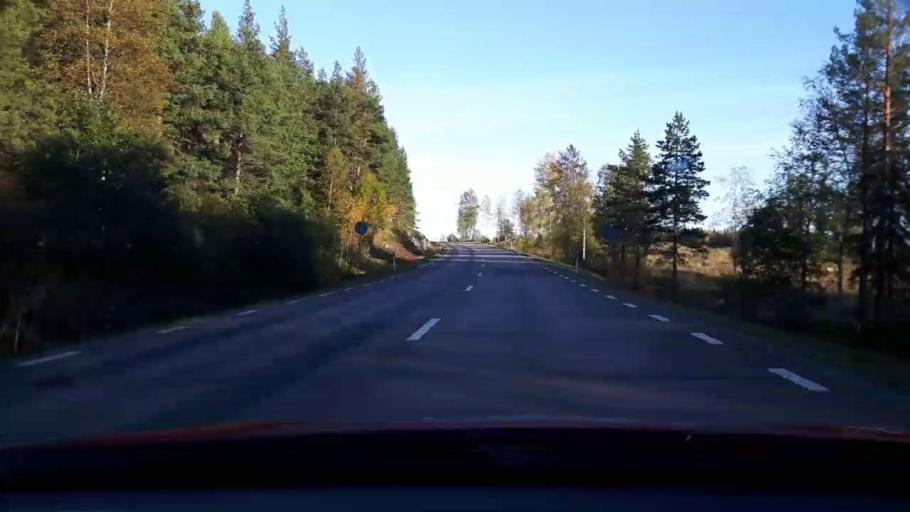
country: SE
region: Jaemtland
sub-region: OEstersunds Kommun
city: Brunflo
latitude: 63.0218
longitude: 14.9252
